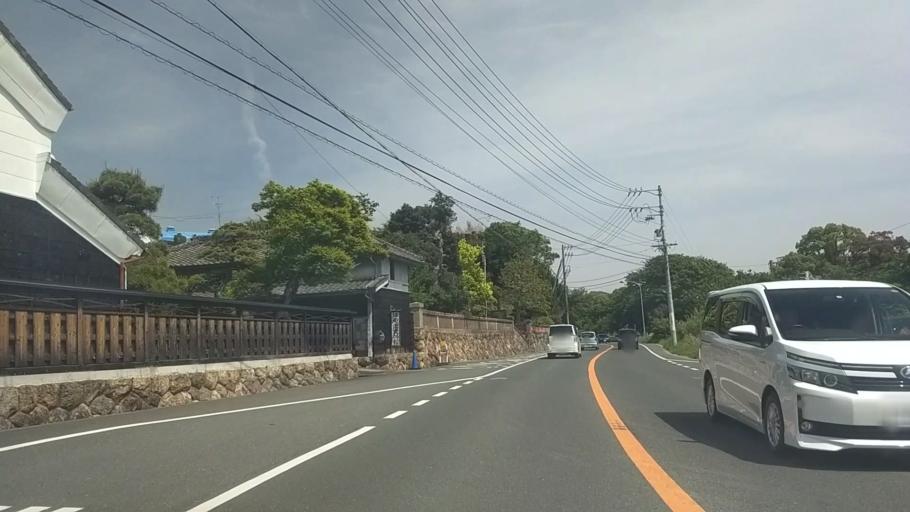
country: JP
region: Shizuoka
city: Kosai-shi
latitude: 34.7896
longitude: 137.5994
